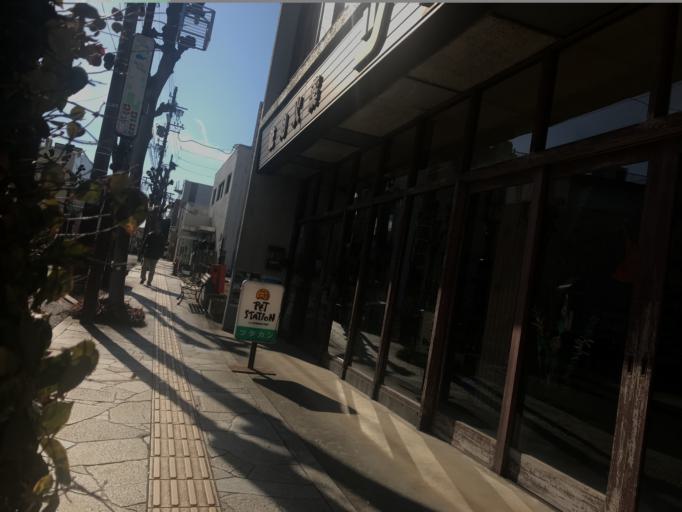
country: JP
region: Gifu
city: Nakatsugawa
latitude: 35.4980
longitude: 137.5054
